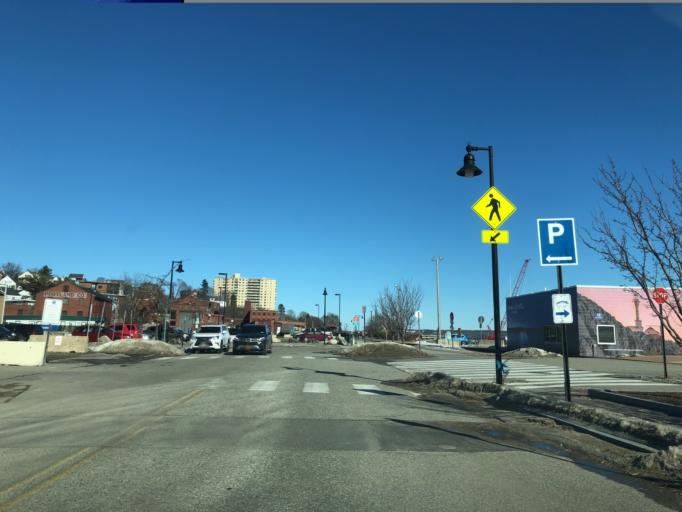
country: US
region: Maine
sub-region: Cumberland County
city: Portland
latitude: 43.6607
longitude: -70.2465
